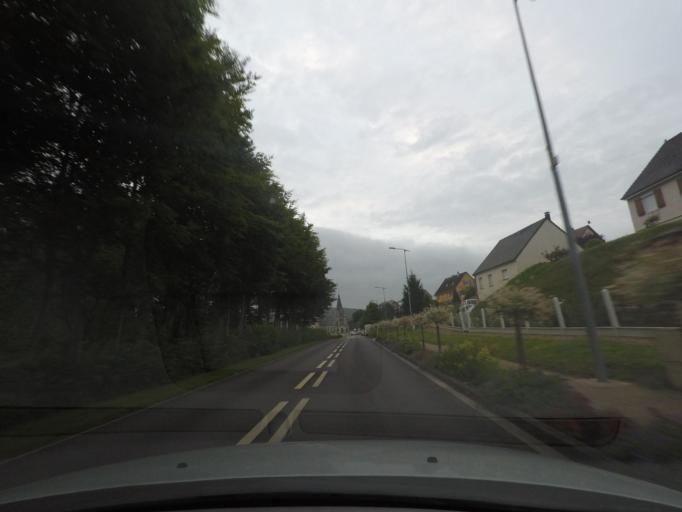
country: FR
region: Haute-Normandie
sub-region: Departement de la Seine-Maritime
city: Fontaine-le-Bourg
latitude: 49.5618
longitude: 1.1577
